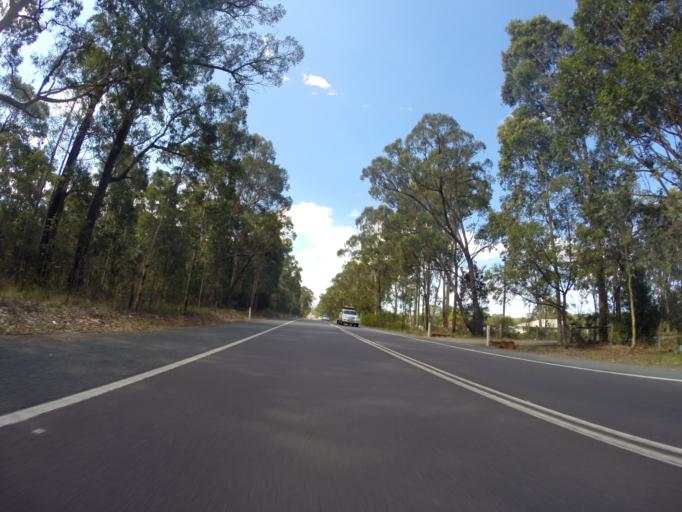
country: AU
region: New South Wales
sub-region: Shoalhaven Shire
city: Falls Creek
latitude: -35.0012
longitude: 150.5833
